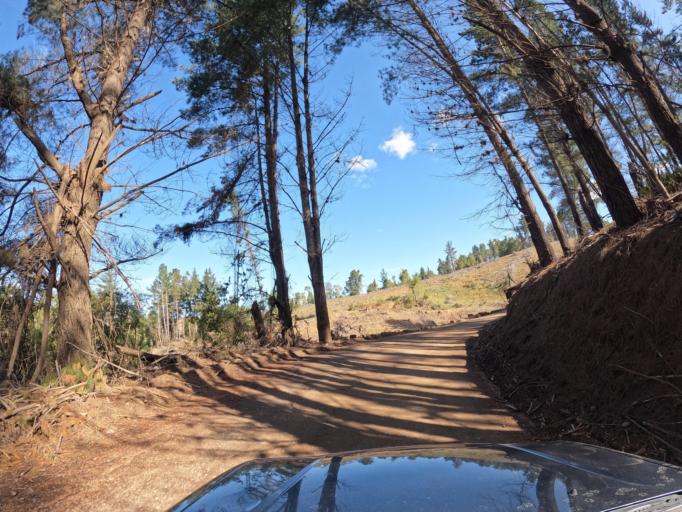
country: CL
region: Biobio
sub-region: Provincia de Biobio
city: La Laja
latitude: -37.0793
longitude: -72.8363
